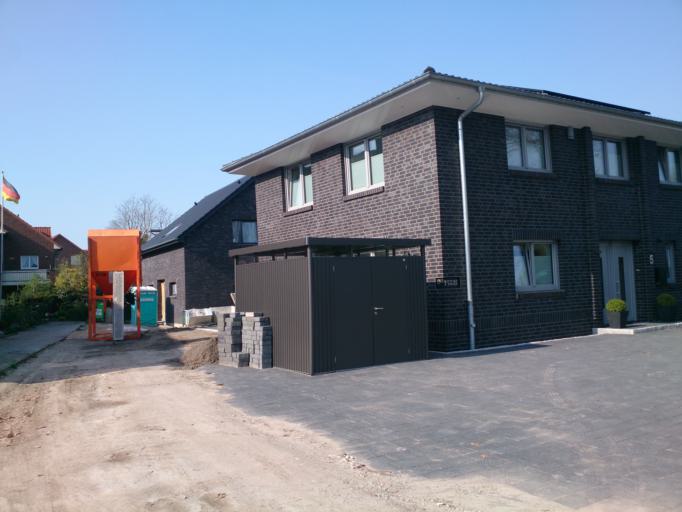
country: DE
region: Lower Saxony
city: Neu Wulmstorf
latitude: 53.4661
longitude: 9.8006
